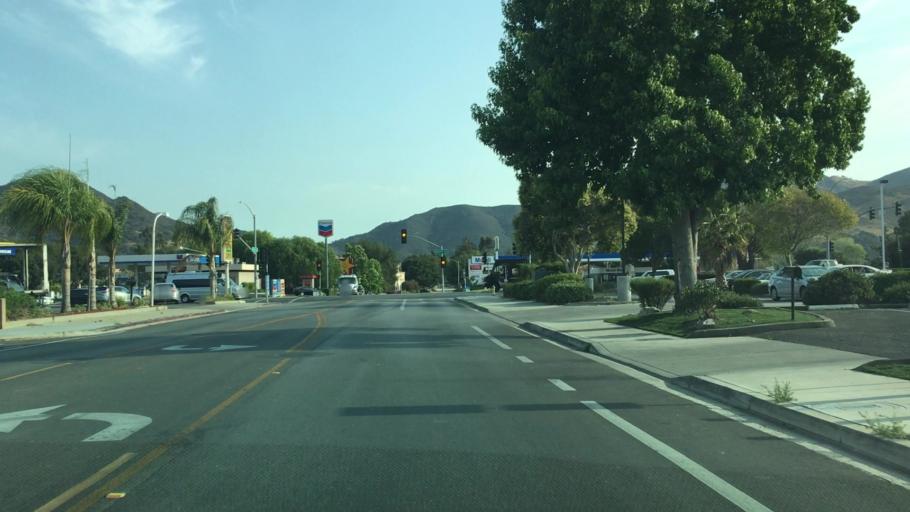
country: US
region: California
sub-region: Santa Barbara County
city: Buellton
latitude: 34.6124
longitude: -120.1887
